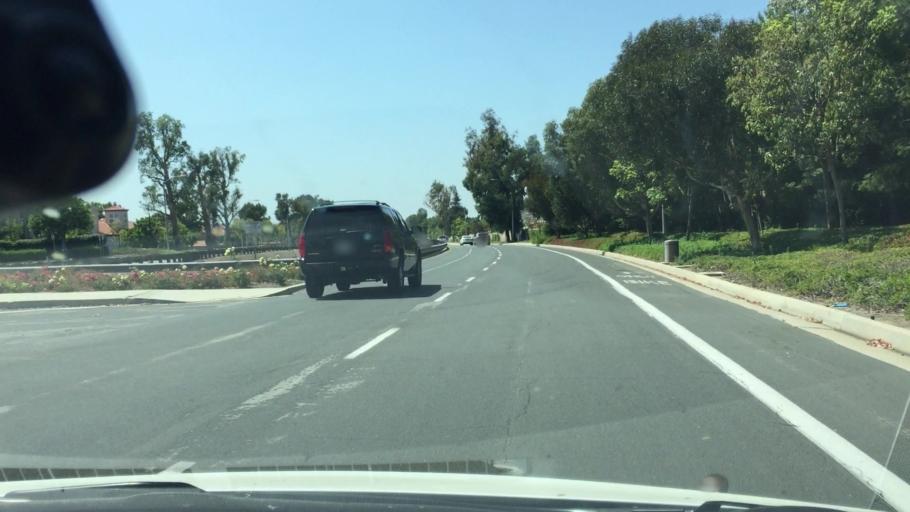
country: US
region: California
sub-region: Orange County
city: Irvine
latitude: 33.6982
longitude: -117.7643
